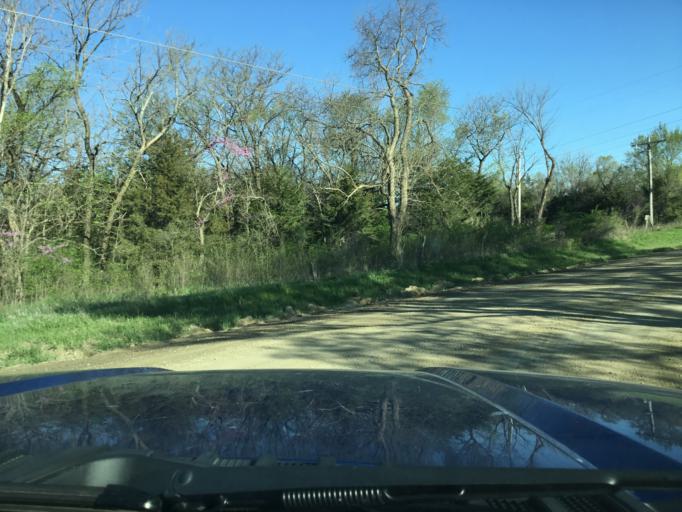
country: US
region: Kansas
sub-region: Douglas County
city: Lawrence
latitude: 38.9569
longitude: -95.3724
